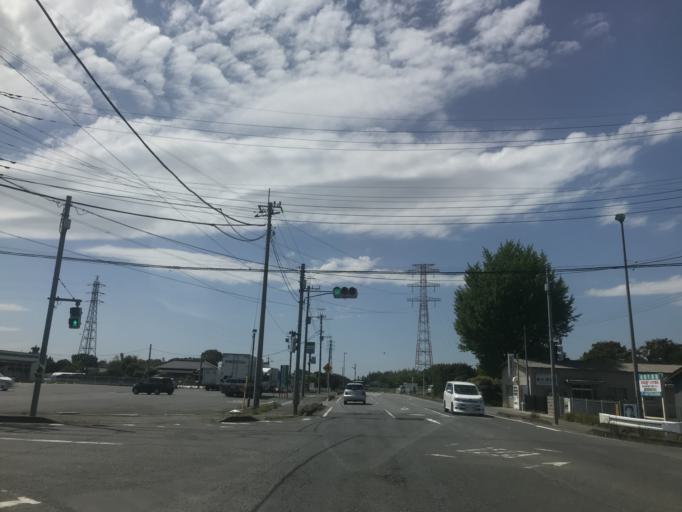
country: JP
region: Chiba
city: Noda
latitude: 35.9678
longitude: 139.8938
